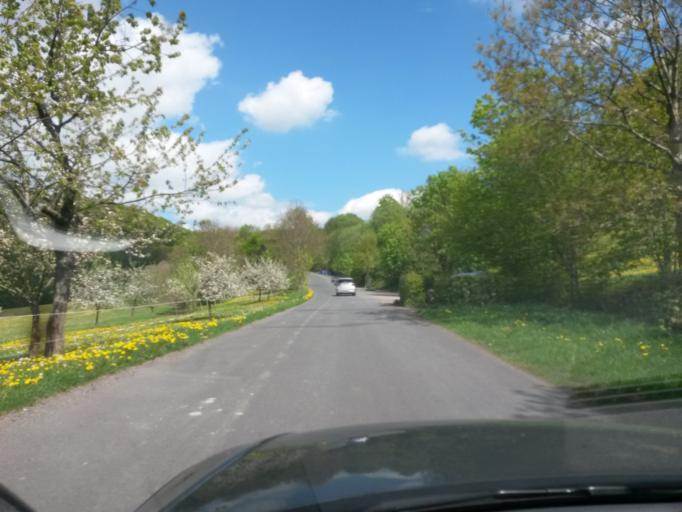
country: DE
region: Hesse
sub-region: Regierungsbezirk Kassel
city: Gersfeld
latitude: 50.4817
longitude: 9.9124
